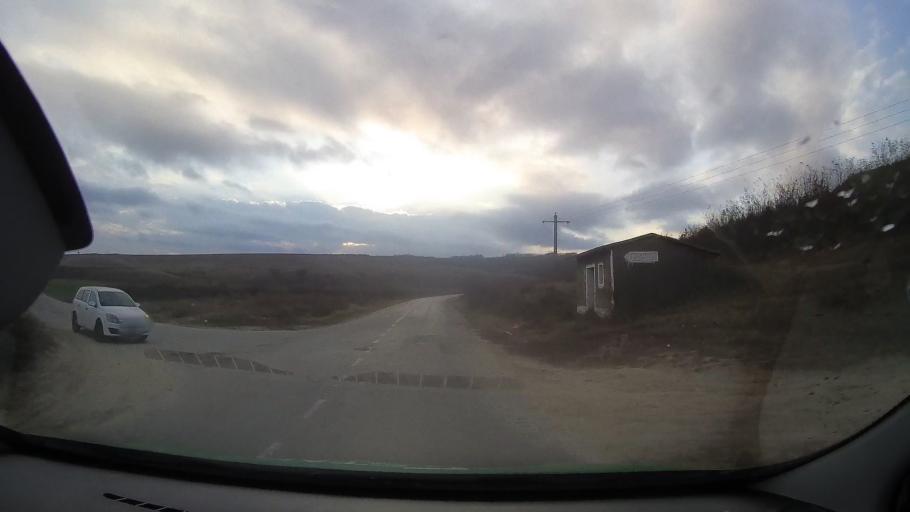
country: RO
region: Constanta
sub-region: Comuna Dobromir
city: Dobromir
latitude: 44.0307
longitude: 27.8316
